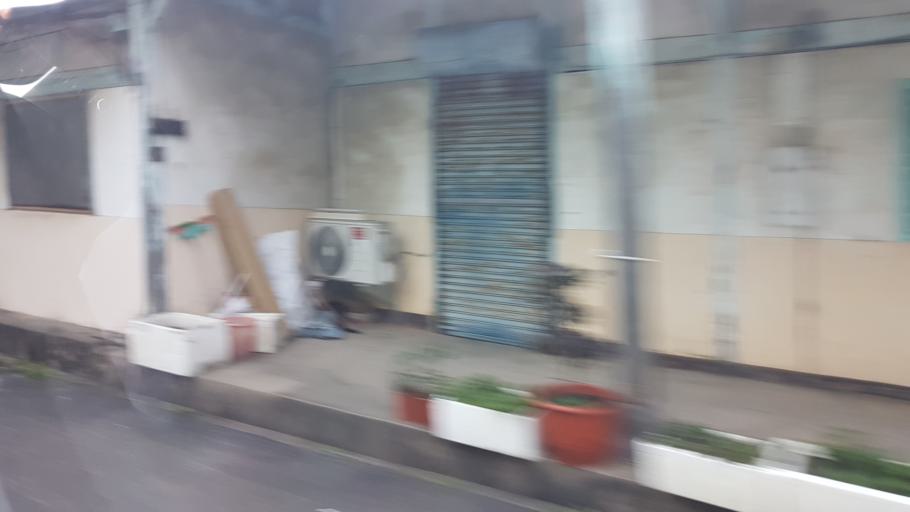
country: TW
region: Taiwan
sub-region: Chiayi
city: Jiayi Shi
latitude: 23.3825
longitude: 120.4391
